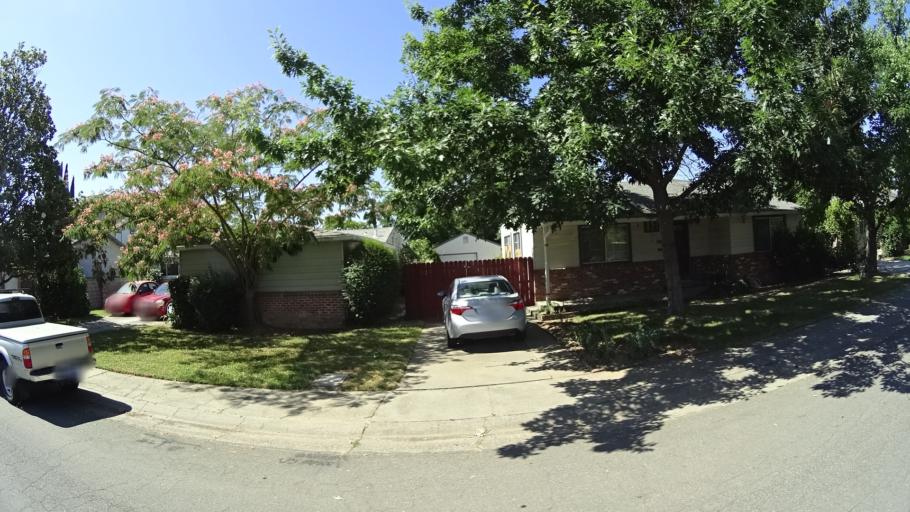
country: US
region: California
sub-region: Sacramento County
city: Parkway
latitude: 38.5255
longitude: -121.5025
